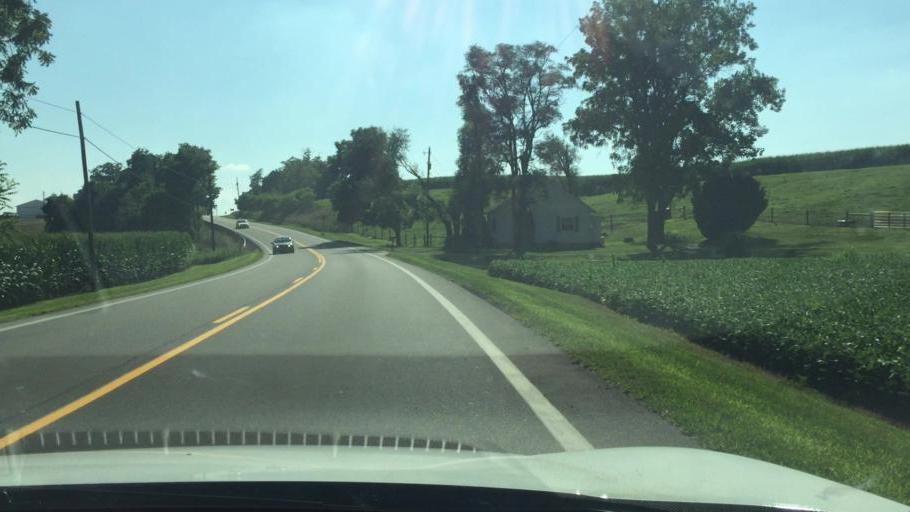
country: US
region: Ohio
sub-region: Clark County
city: Northridge
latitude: 40.0203
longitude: -83.6699
